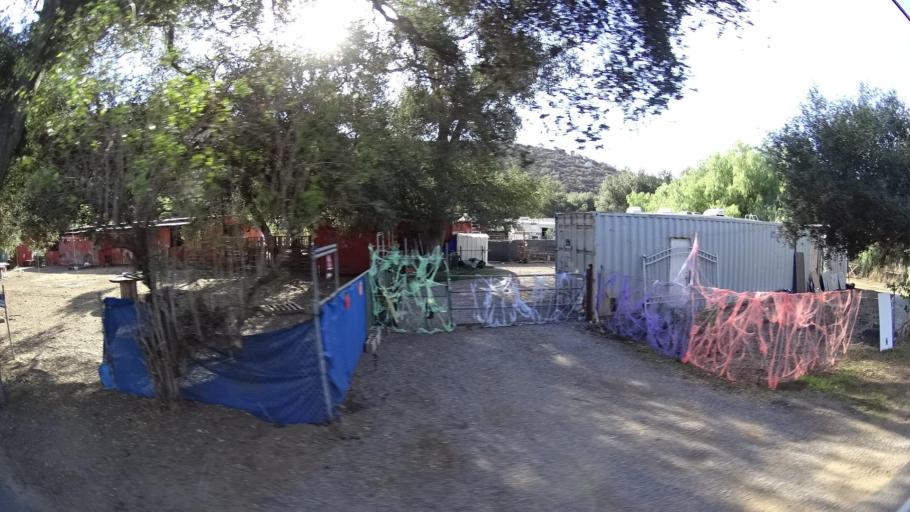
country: US
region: California
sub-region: San Diego County
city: Harbison Canyon
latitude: 32.7995
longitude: -116.8254
